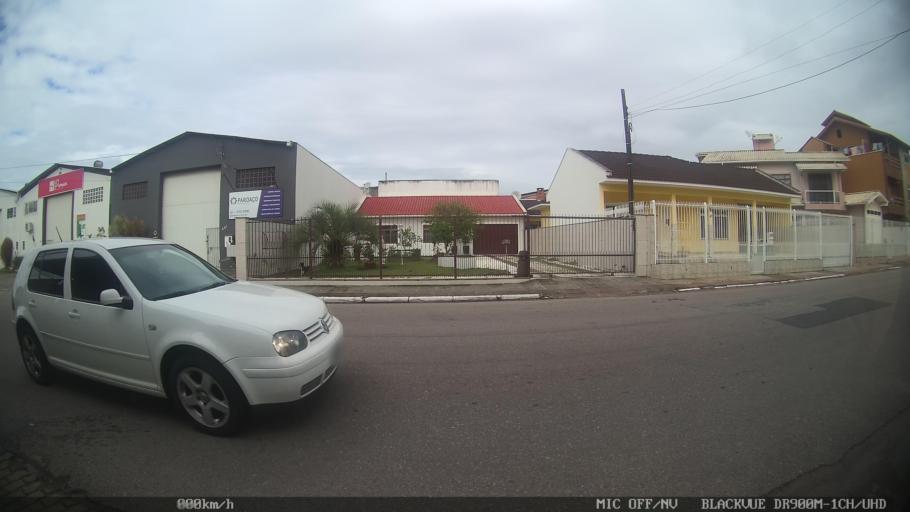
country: BR
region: Santa Catarina
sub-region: Sao Jose
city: Campinas
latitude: -27.5505
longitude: -48.6252
